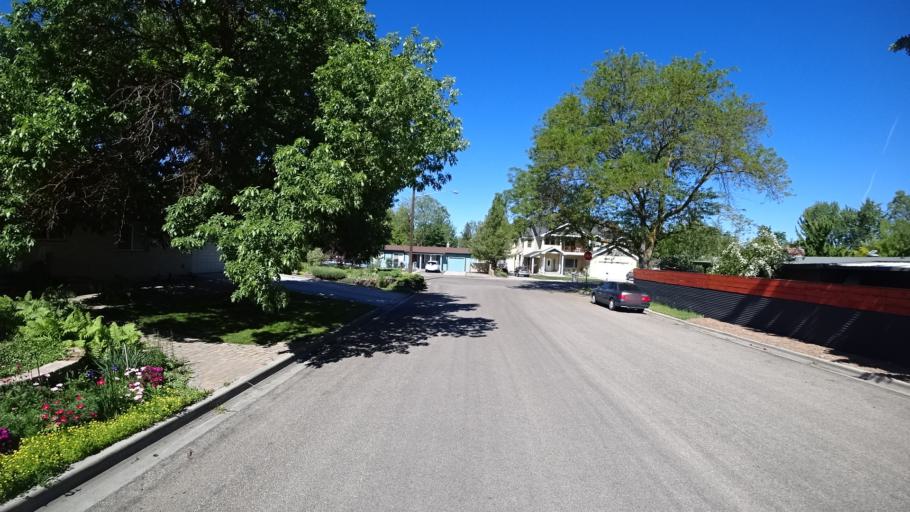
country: US
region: Idaho
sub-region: Ada County
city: Garden City
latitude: 43.6427
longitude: -116.2280
